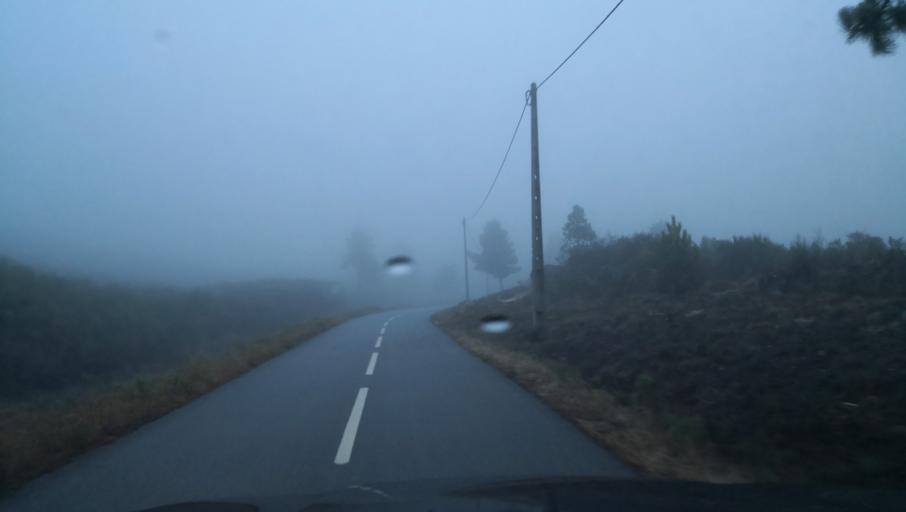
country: PT
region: Vila Real
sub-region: Sabrosa
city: Sabrosa
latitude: 41.2831
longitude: -7.5977
